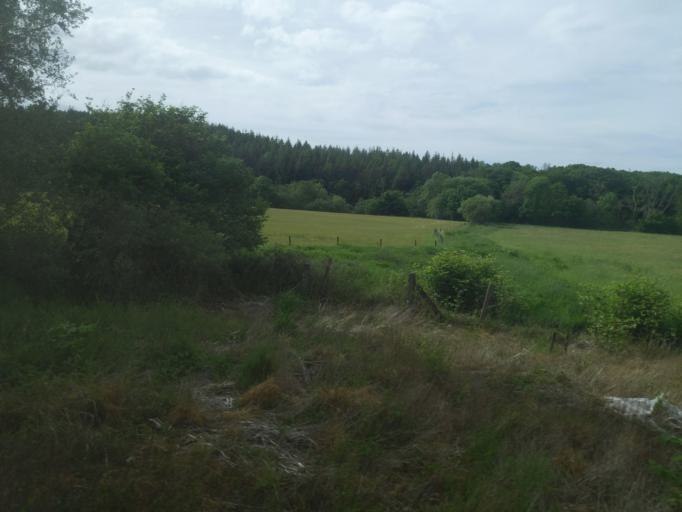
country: GB
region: England
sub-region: Devon
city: Winkleigh
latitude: 50.9577
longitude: -3.9478
